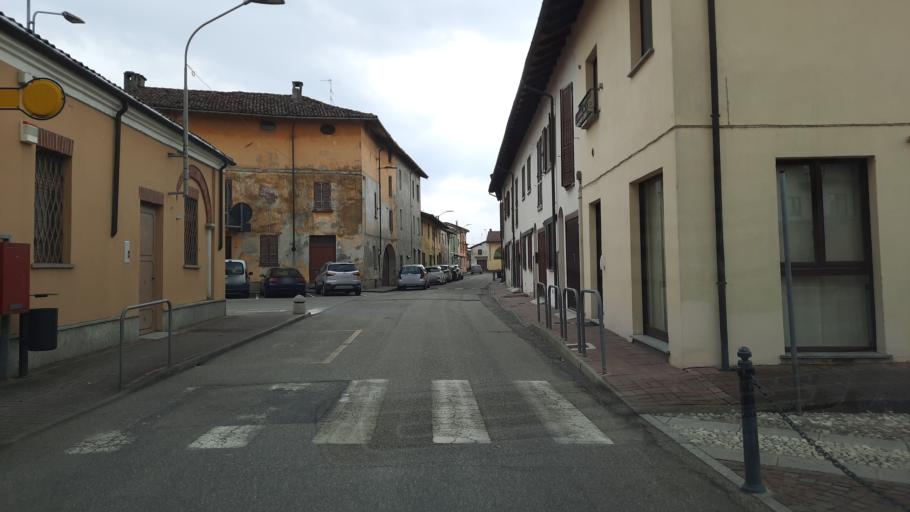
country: IT
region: Lombardy
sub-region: Provincia di Pavia
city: Castelnovetto
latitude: 45.2543
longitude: 8.6118
